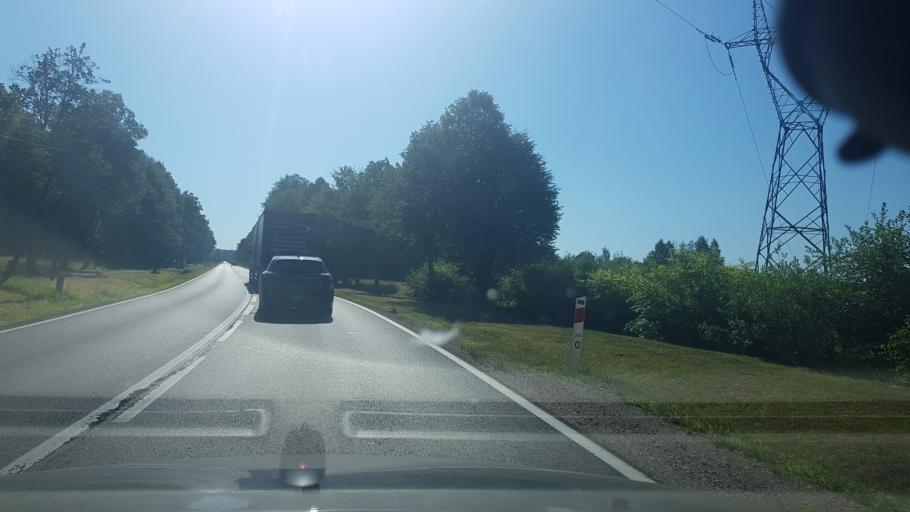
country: PL
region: Masovian Voivodeship
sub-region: Powiat wegrowski
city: Lochow
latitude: 52.5401
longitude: 21.6525
